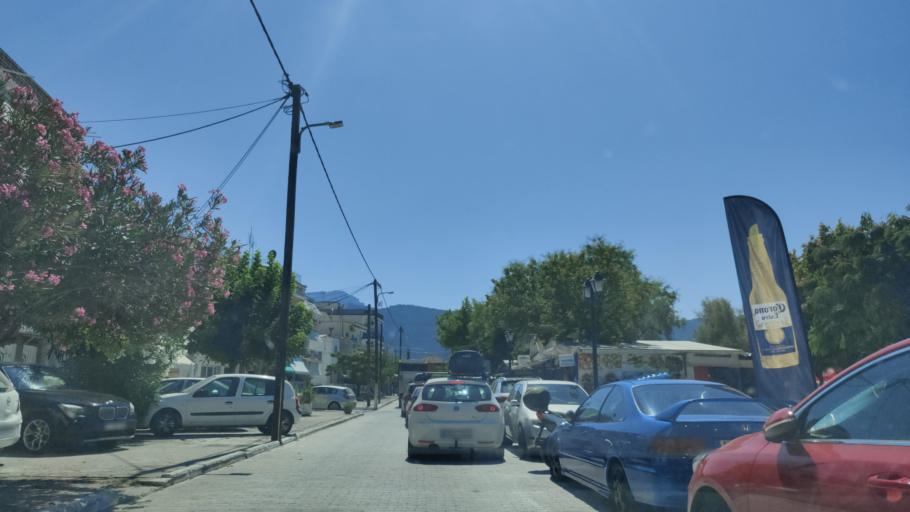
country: GR
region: East Macedonia and Thrace
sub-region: Nomos Kavalas
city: Thasos
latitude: 40.7826
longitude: 24.7148
